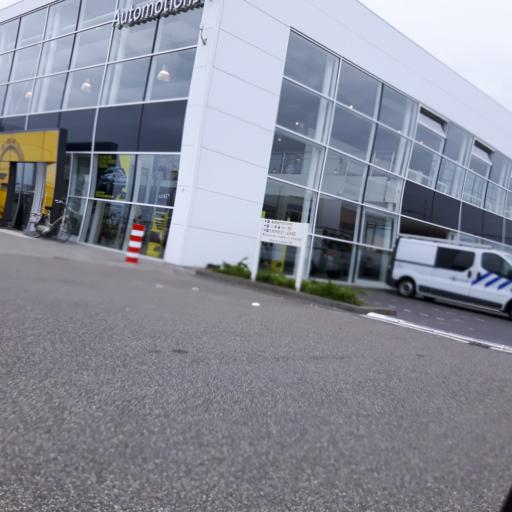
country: NL
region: Zeeland
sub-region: Gemeente Goes
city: Goes
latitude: 51.4843
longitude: 3.8779
